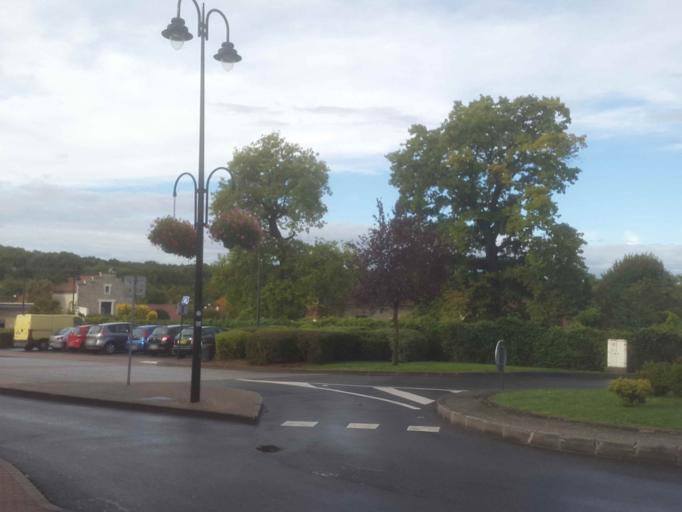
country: FR
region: Ile-de-France
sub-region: Departement du Val-d'Oise
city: Mery-sur-Oise
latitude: 49.0578
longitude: 2.1909
